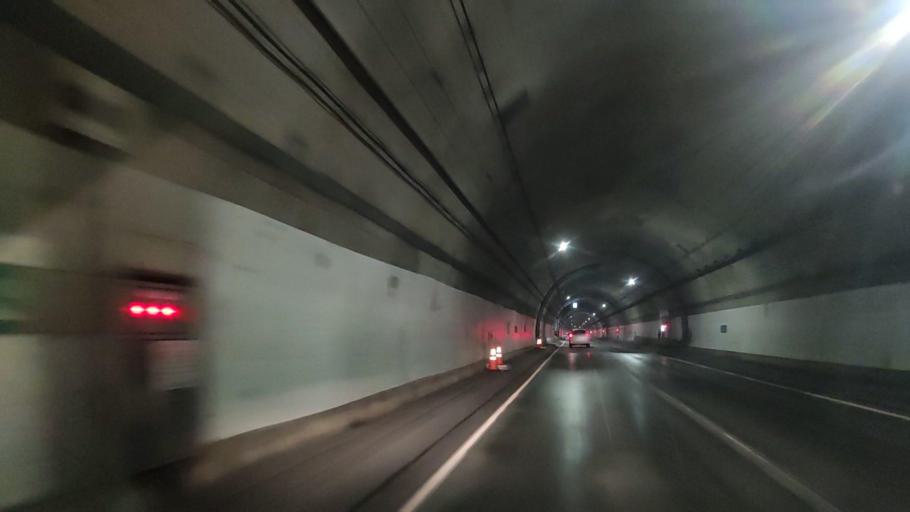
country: JP
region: Hokkaido
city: Rumoi
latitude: 43.7058
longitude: 141.3349
